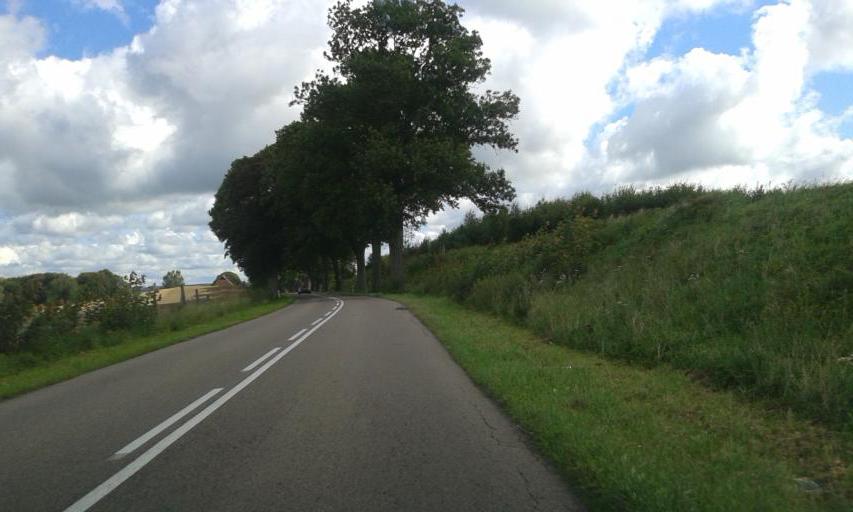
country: PL
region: West Pomeranian Voivodeship
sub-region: Powiat koszalinski
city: Bobolice
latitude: 53.9800
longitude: 16.6725
